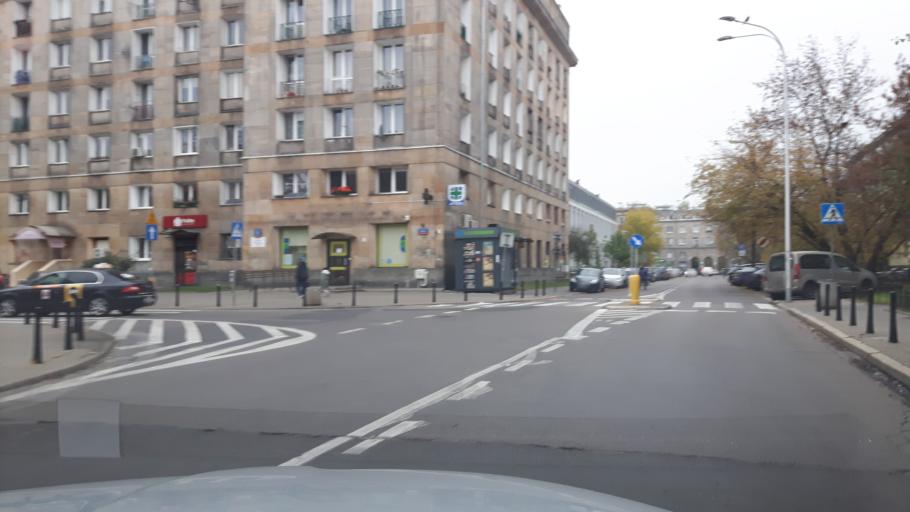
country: PL
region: Masovian Voivodeship
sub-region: Warszawa
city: Praga Polnoc
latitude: 52.2616
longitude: 21.0307
